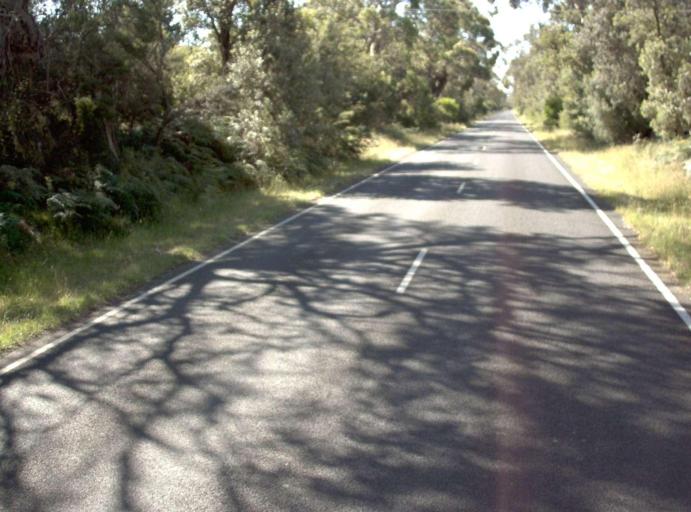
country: AU
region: Victoria
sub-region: Latrobe
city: Traralgon
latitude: -38.6606
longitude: 146.6835
